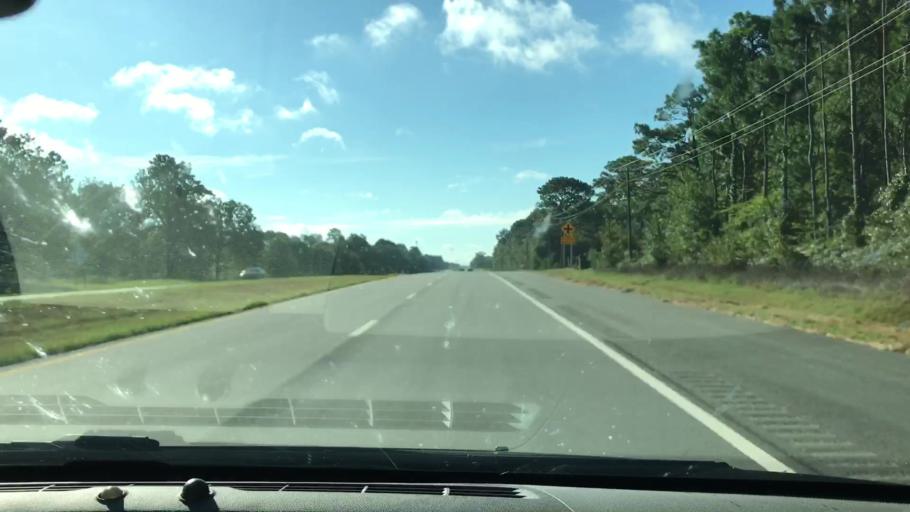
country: US
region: Georgia
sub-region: Lee County
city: Leesburg
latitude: 31.6701
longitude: -84.2877
